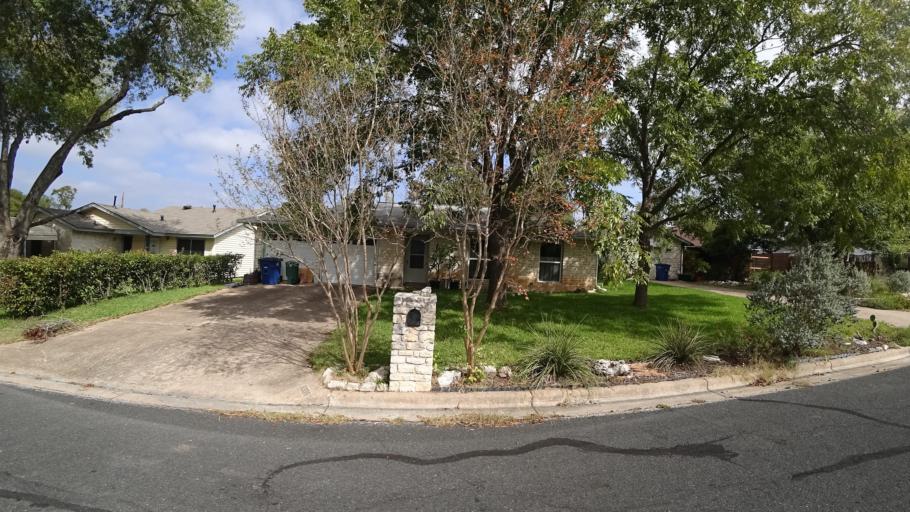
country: US
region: Texas
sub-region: Travis County
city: Shady Hollow
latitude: 30.1997
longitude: -97.8326
